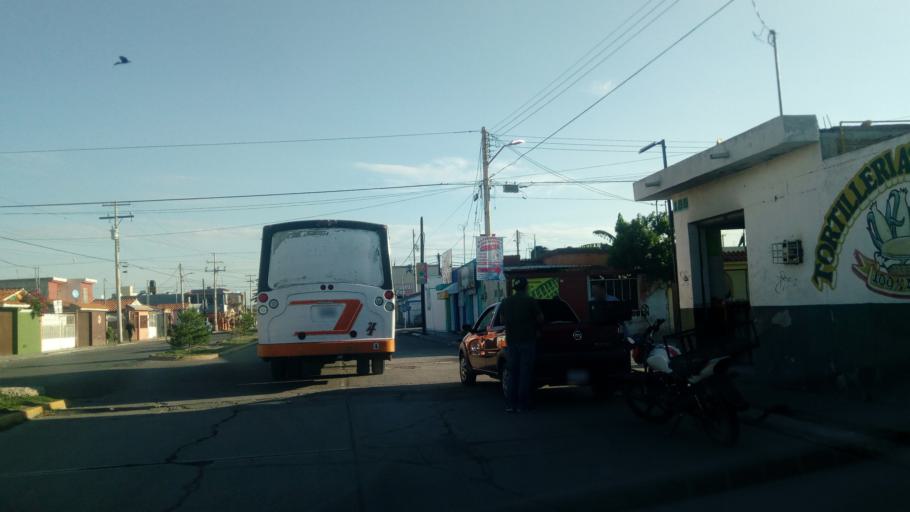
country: MX
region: Durango
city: Victoria de Durango
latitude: 24.0601
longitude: -104.5848
